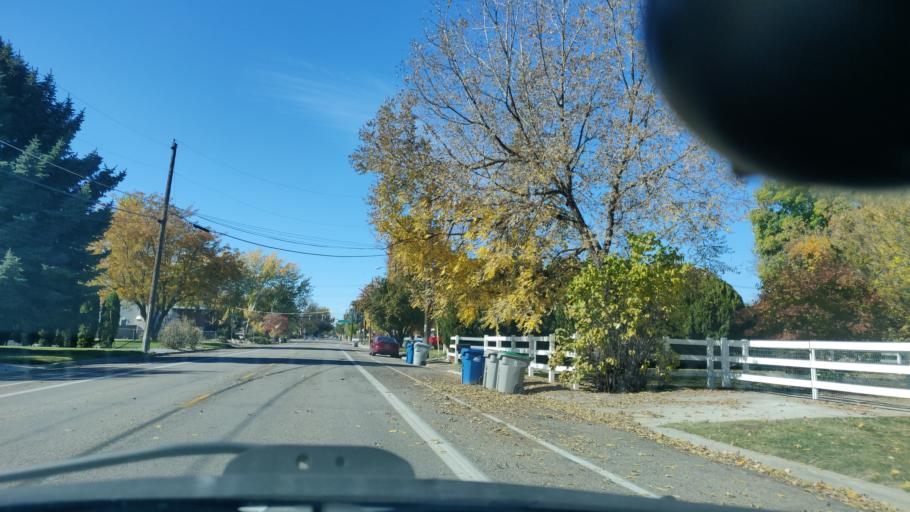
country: US
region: Idaho
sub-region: Ada County
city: Garden City
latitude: 43.5934
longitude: -116.2313
